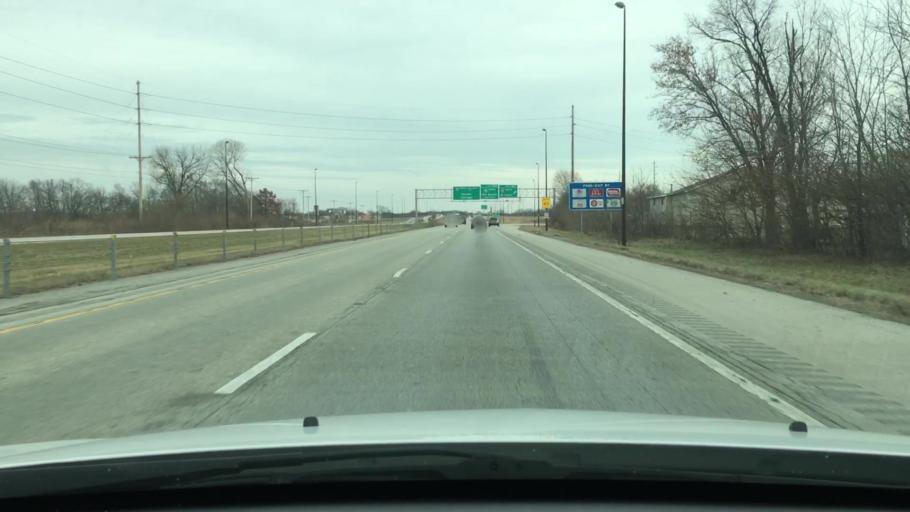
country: US
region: Illinois
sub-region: Sangamon County
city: Southern View
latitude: 39.7426
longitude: -89.6530
